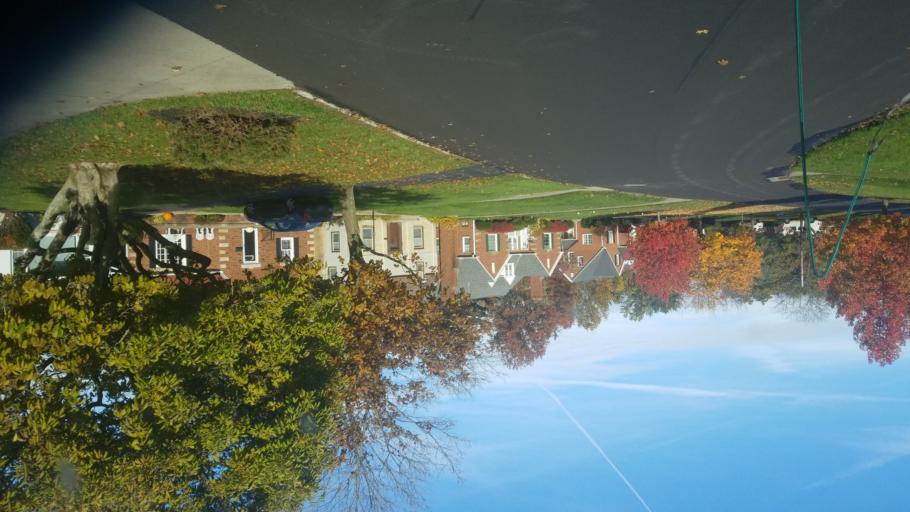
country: US
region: Ohio
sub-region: Richland County
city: Mansfield
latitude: 40.7404
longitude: -82.5307
